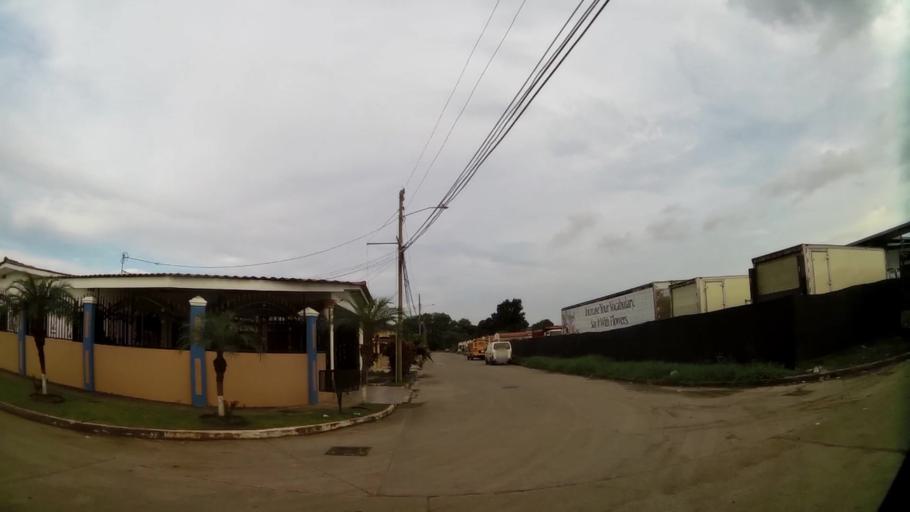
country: PA
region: Panama
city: Tocumen
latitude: 9.0931
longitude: -79.3872
